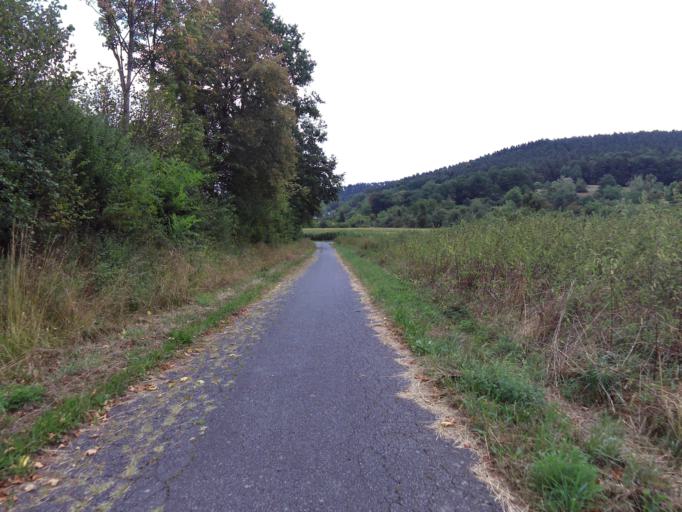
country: DE
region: Hesse
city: Hochst im Odenwald
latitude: 49.8150
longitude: 9.0269
